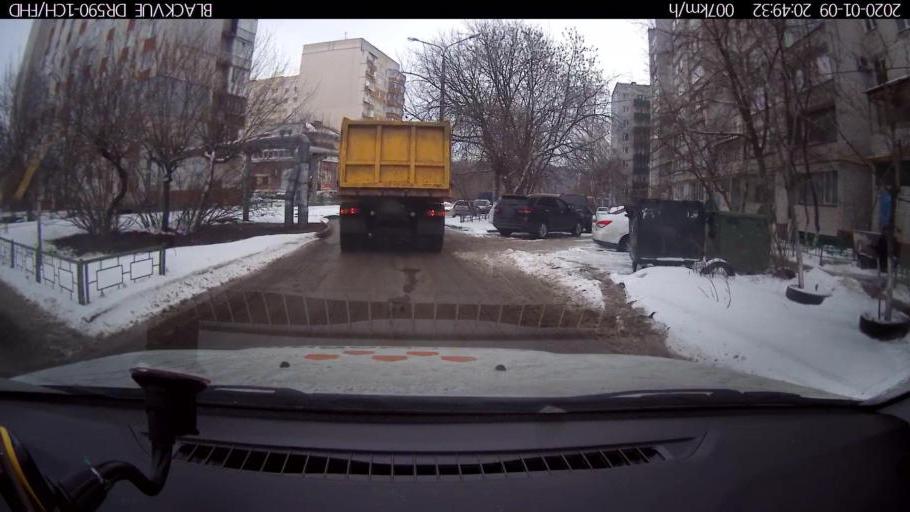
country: RU
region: Nizjnij Novgorod
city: Nizhniy Novgorod
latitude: 56.2904
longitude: 43.9425
